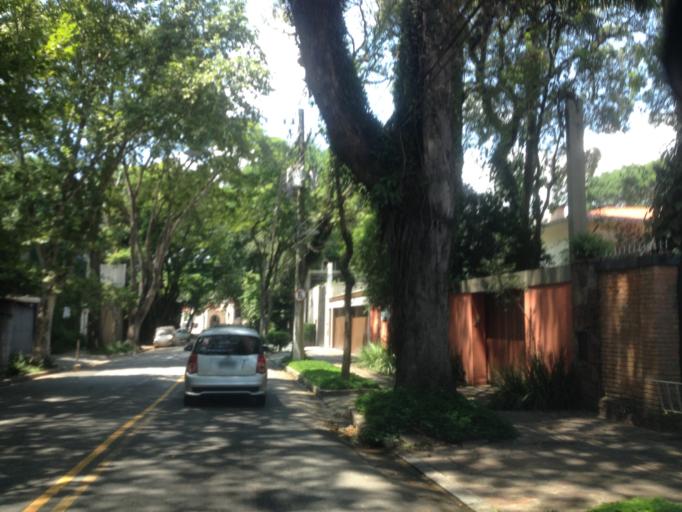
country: BR
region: Sao Paulo
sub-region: Sao Paulo
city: Sao Paulo
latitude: -23.5729
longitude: -46.6808
